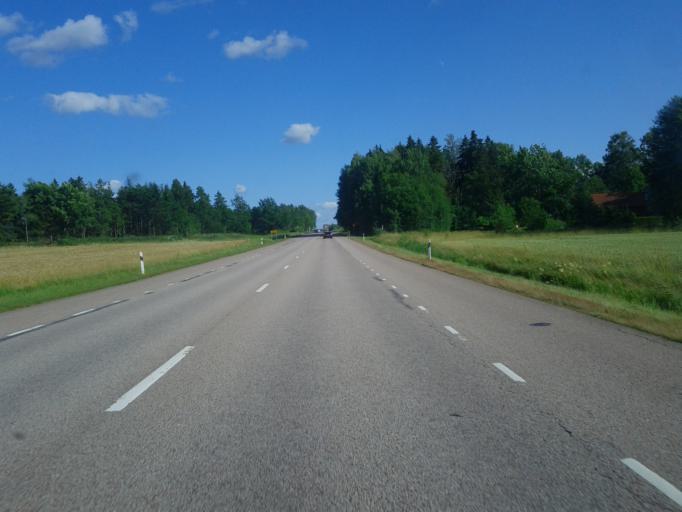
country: SE
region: Uppsala
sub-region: Enkopings Kommun
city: Enkoping
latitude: 59.6766
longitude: 17.0503
